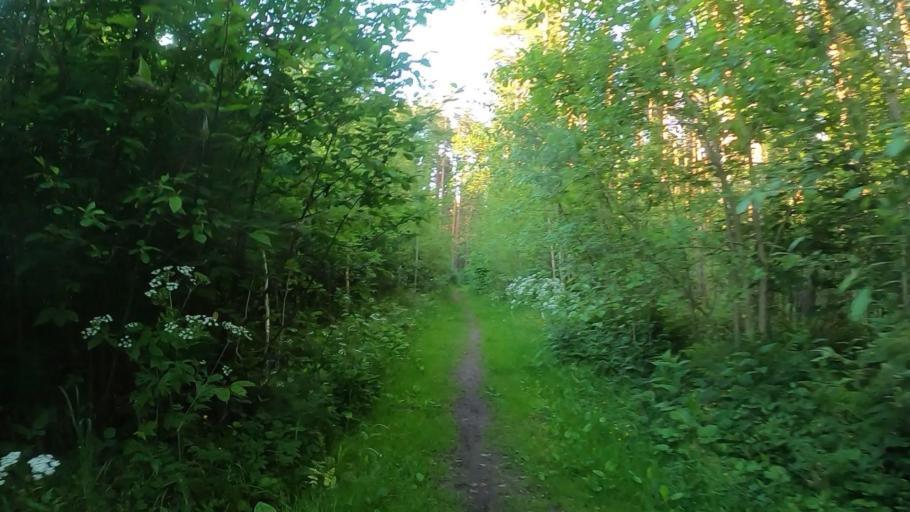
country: LV
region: Marupe
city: Marupe
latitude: 56.8843
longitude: 24.0290
